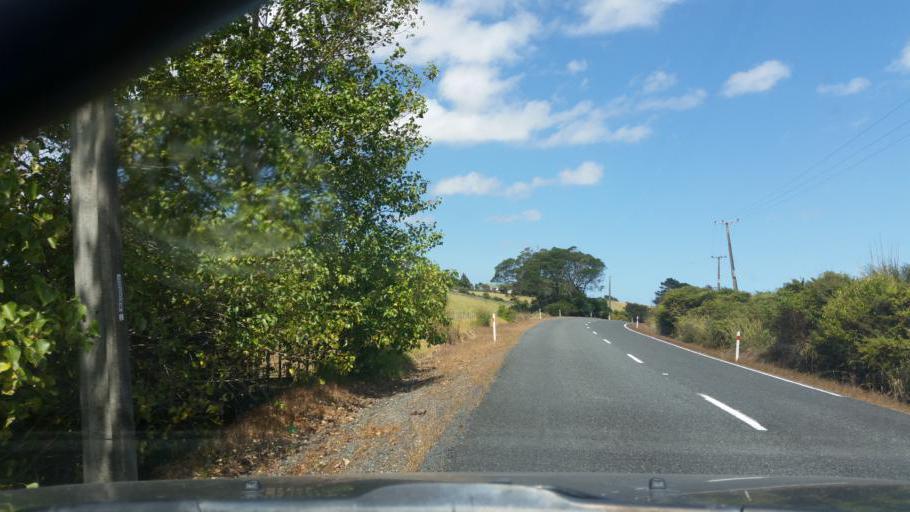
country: NZ
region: Northland
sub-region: Kaipara District
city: Dargaville
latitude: -35.9077
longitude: 173.8440
